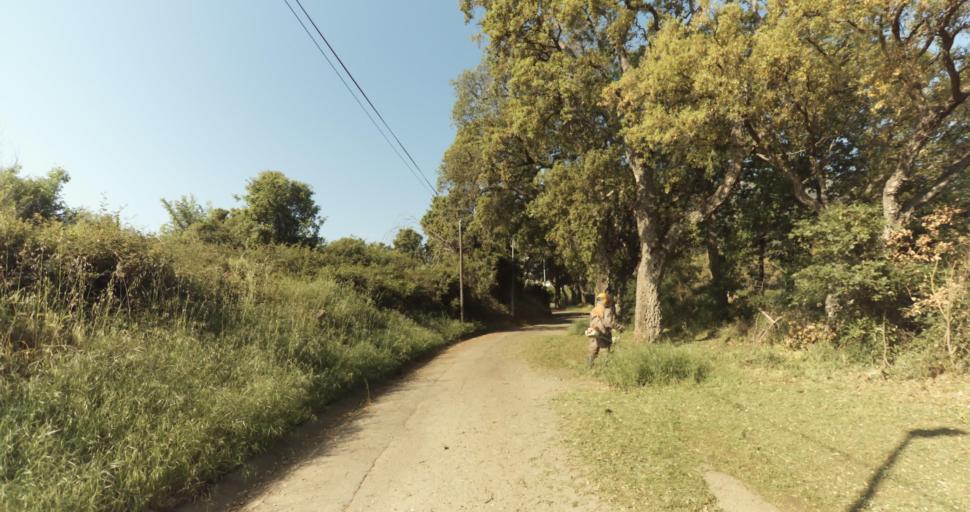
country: FR
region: Corsica
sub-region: Departement de la Haute-Corse
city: Biguglia
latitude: 42.6329
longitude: 9.4284
